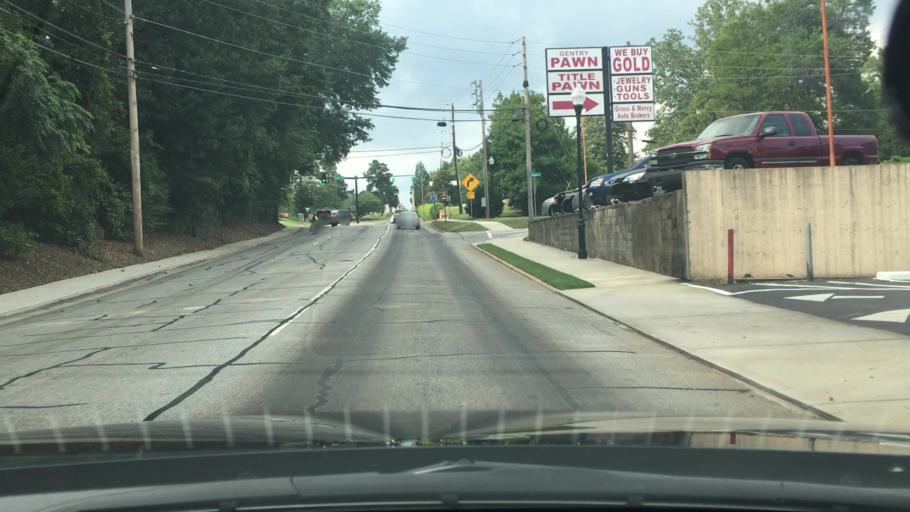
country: US
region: Georgia
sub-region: Coweta County
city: Newnan
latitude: 33.3794
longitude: -84.7990
